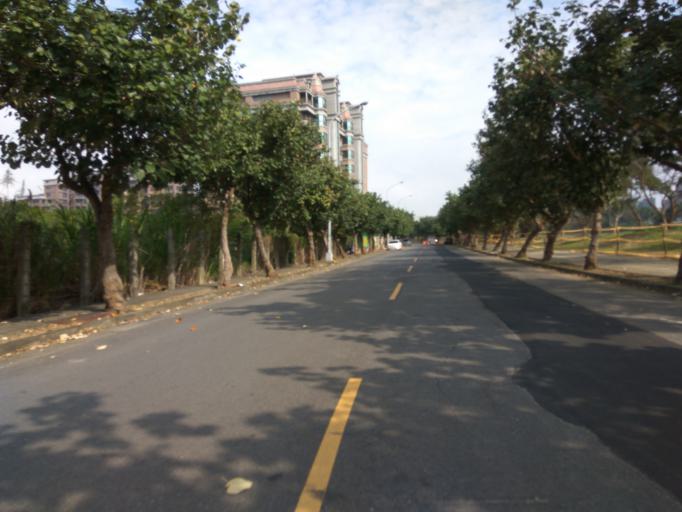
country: TW
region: Taiwan
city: Taoyuan City
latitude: 25.0160
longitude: 121.2233
